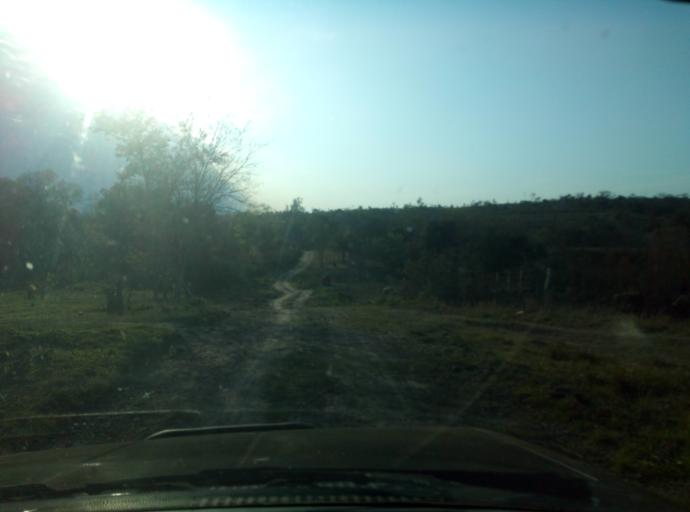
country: PY
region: Caaguazu
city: Yhu
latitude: -25.1989
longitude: -56.1149
